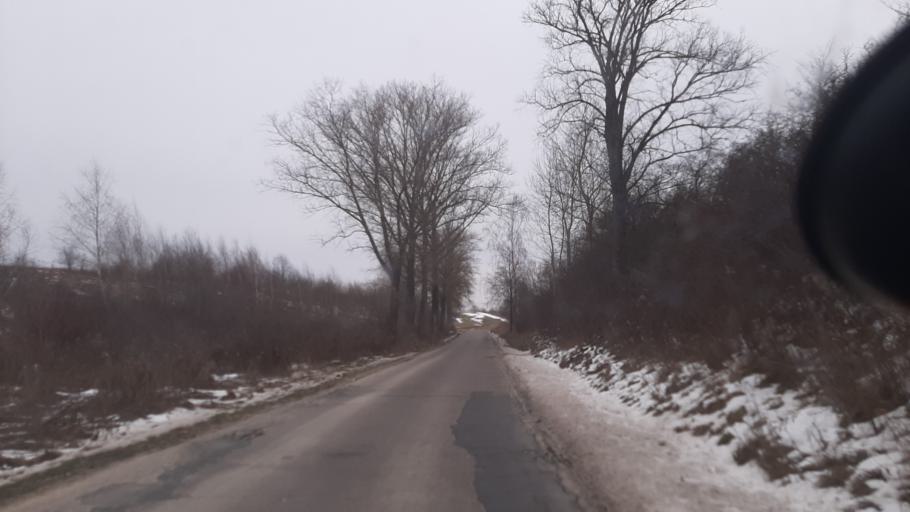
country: PL
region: Lublin Voivodeship
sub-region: Powiat lubelski
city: Jakubowice Murowane
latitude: 51.2847
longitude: 22.6113
